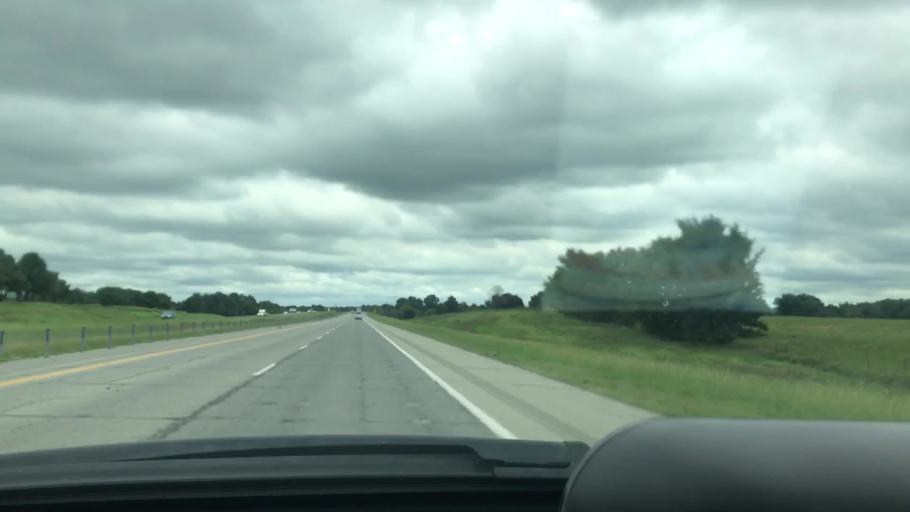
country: US
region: Oklahoma
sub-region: McIntosh County
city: Checotah
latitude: 35.5456
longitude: -95.5015
